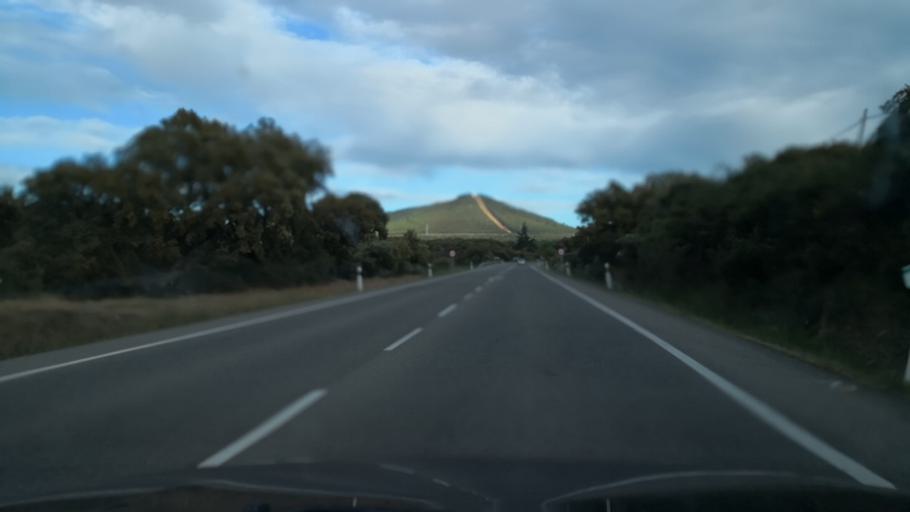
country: ES
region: Extremadura
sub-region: Provincia de Caceres
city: Pedroso de Acim
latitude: 39.8327
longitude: -6.3867
